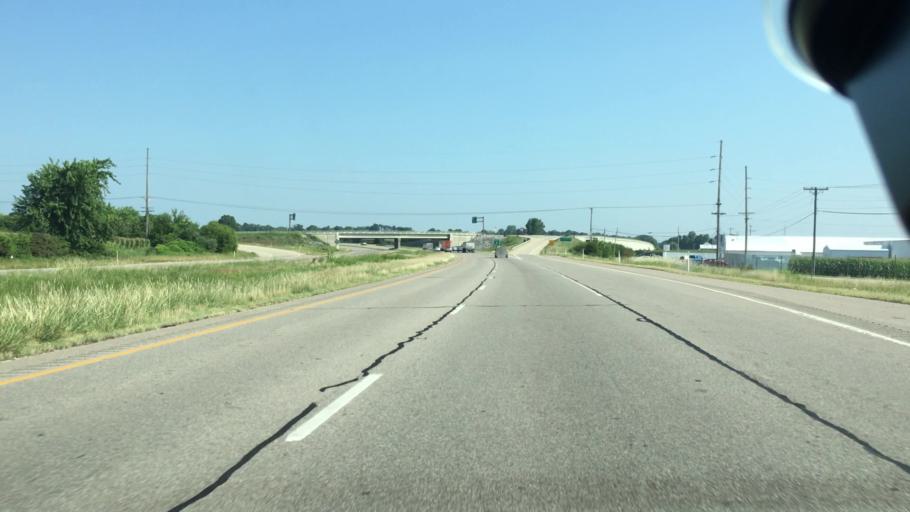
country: US
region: Indiana
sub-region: Gibson County
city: Princeton
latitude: 38.3091
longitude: -87.5674
